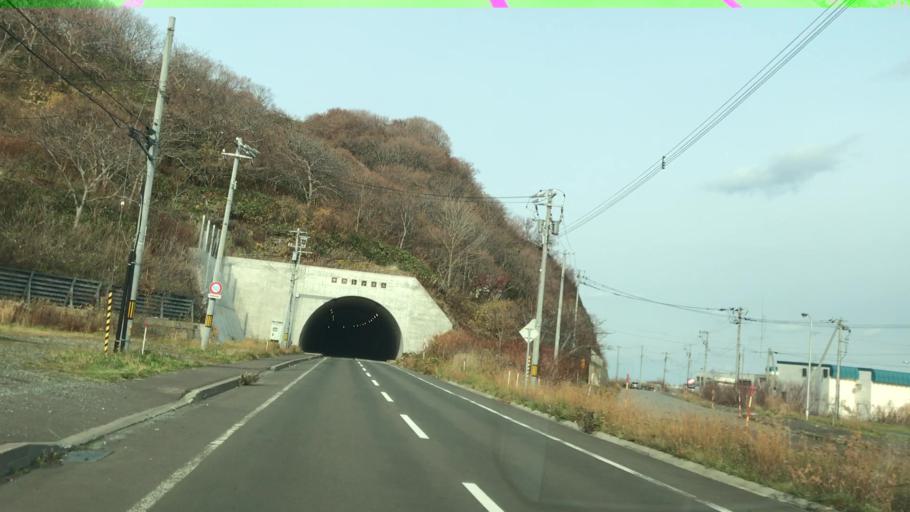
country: JP
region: Hokkaido
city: Iwanai
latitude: 43.3286
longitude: 140.3784
